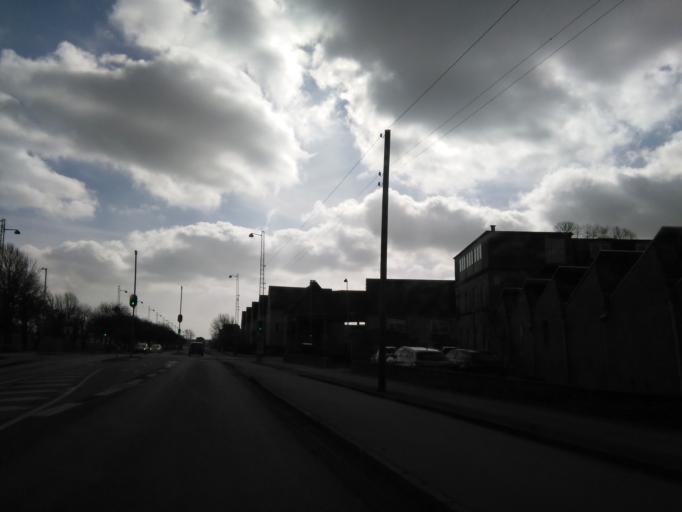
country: DK
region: Capital Region
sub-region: Tarnby Kommune
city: Tarnby
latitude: 55.6398
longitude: 12.6476
